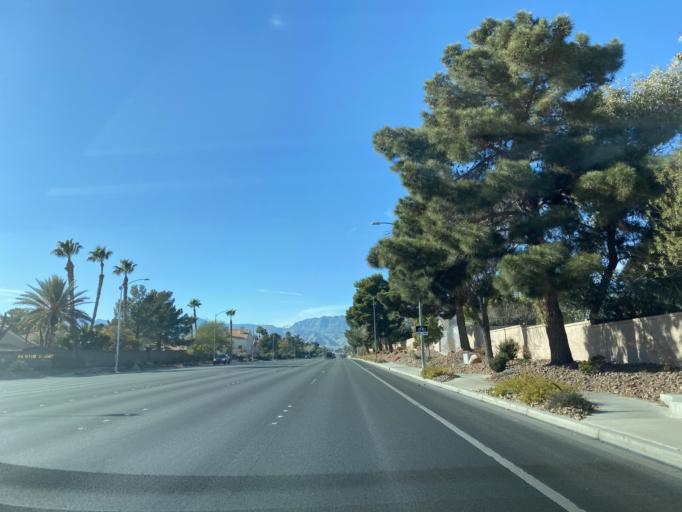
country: US
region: Nevada
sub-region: Clark County
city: Las Vegas
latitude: 36.2631
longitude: -115.2626
